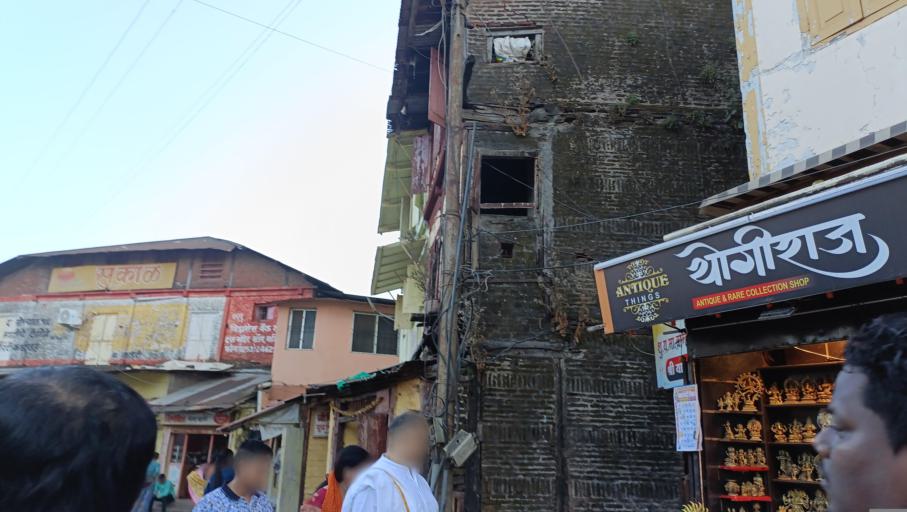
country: IN
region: Maharashtra
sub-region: Nashik Division
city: Trimbak
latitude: 19.9329
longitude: 73.5294
